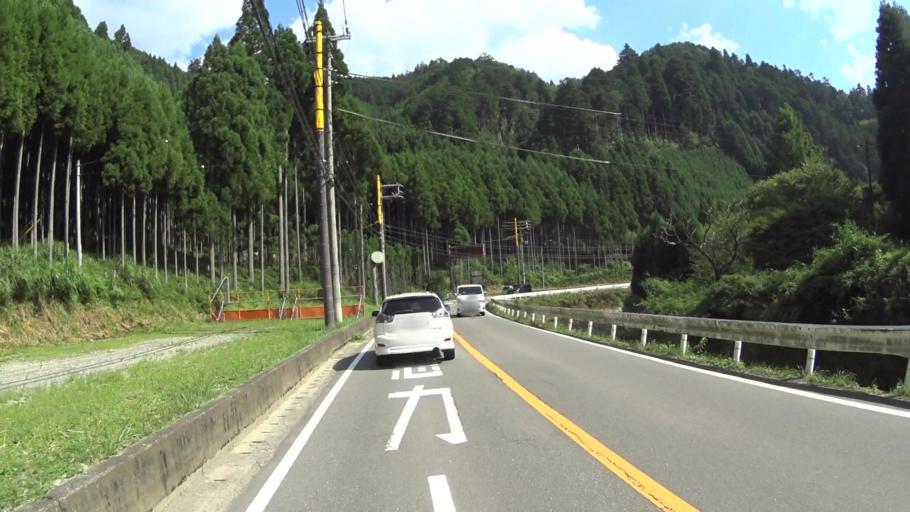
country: JP
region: Kyoto
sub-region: Kyoto-shi
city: Kamigyo-ku
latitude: 35.1075
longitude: 135.6796
